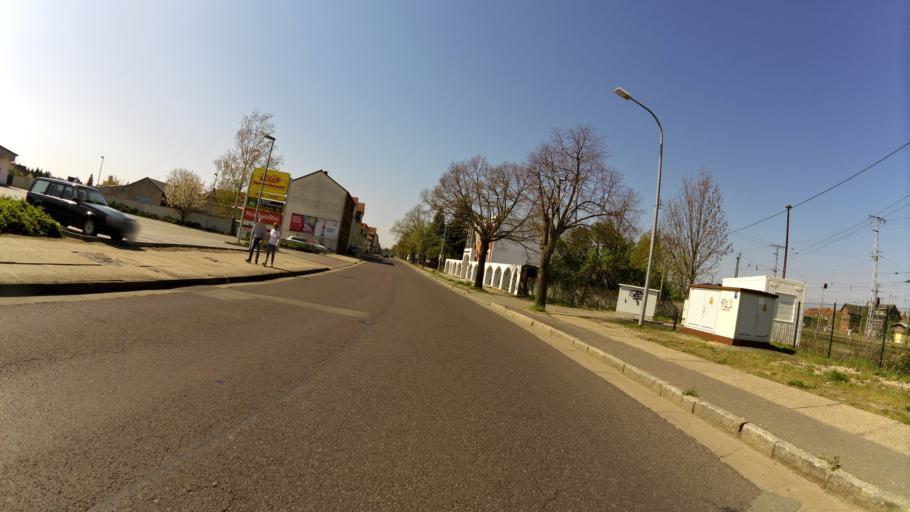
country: DE
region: Saxony-Anhalt
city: Stendal
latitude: 52.5941
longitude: 11.8543
